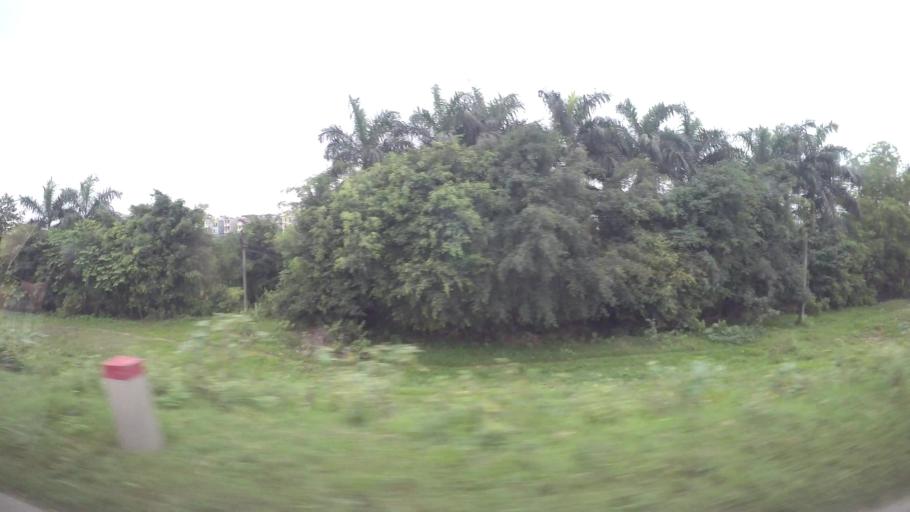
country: VN
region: Ha Noi
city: Trau Quy
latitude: 21.0667
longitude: 105.9182
